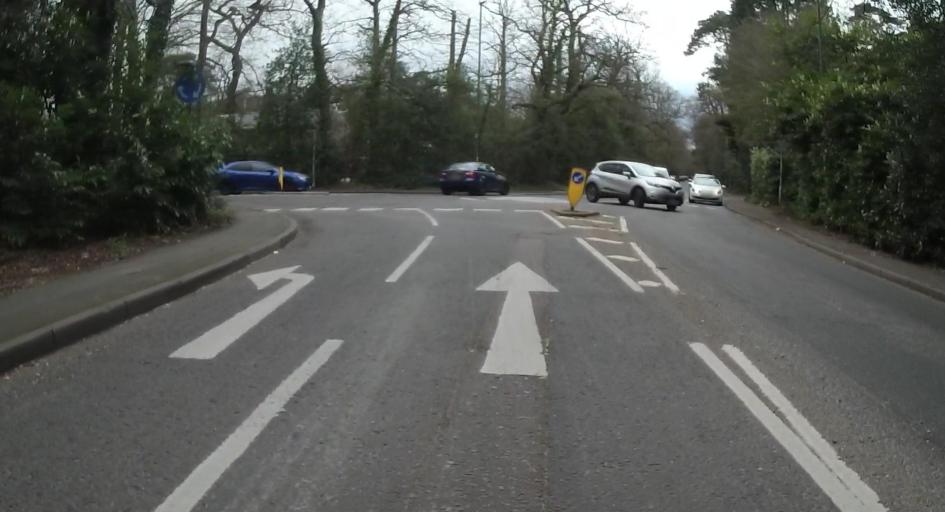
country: GB
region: England
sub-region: Surrey
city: West Byfleet
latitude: 51.3409
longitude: -0.5205
